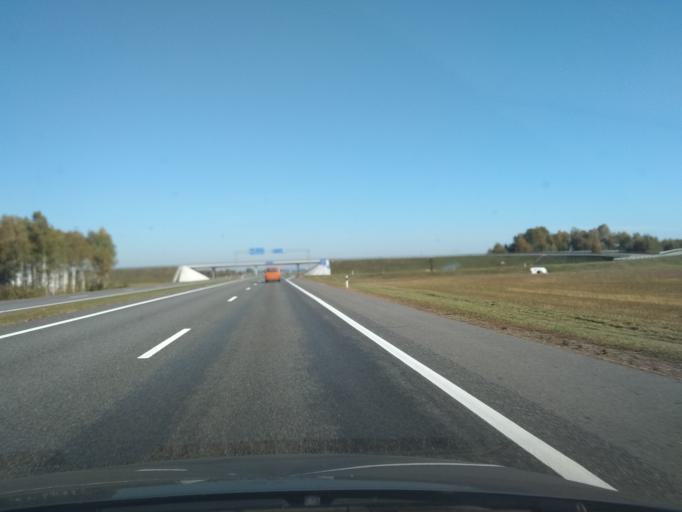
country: BY
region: Brest
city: Antopal'
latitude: 52.3052
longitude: 24.5943
